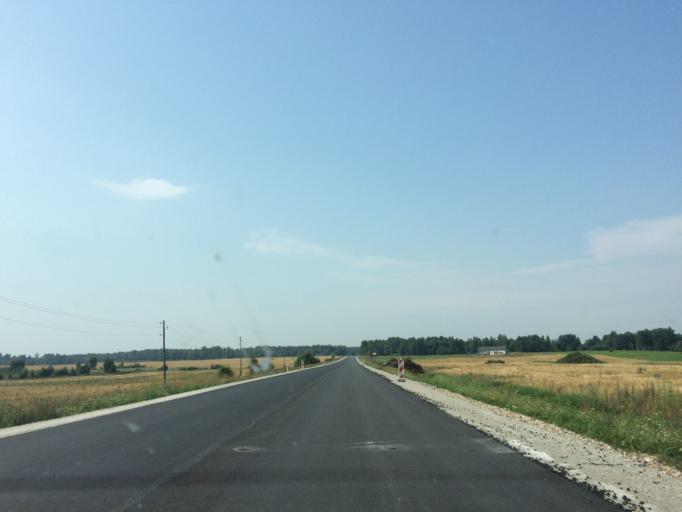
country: LV
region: Rezekne
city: Rezekne
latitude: 56.5222
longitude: 27.5162
